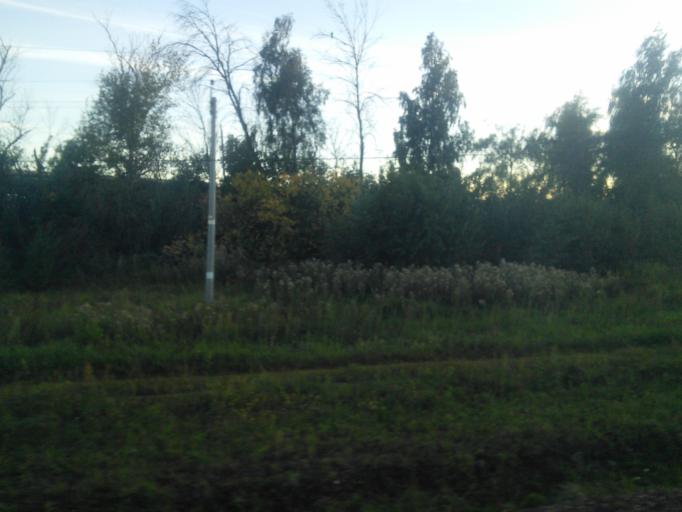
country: RU
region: Moskovskaya
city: Kupavna
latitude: 55.7397
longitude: 38.1687
